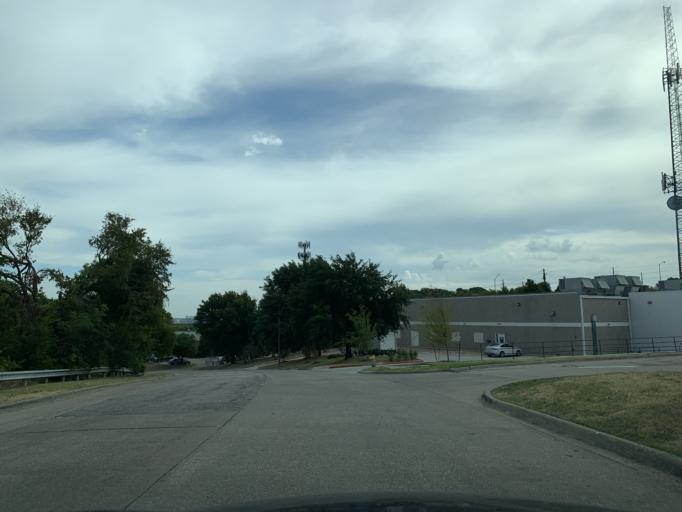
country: US
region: Texas
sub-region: Dallas County
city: Cockrell Hill
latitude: 32.7688
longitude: -96.8587
